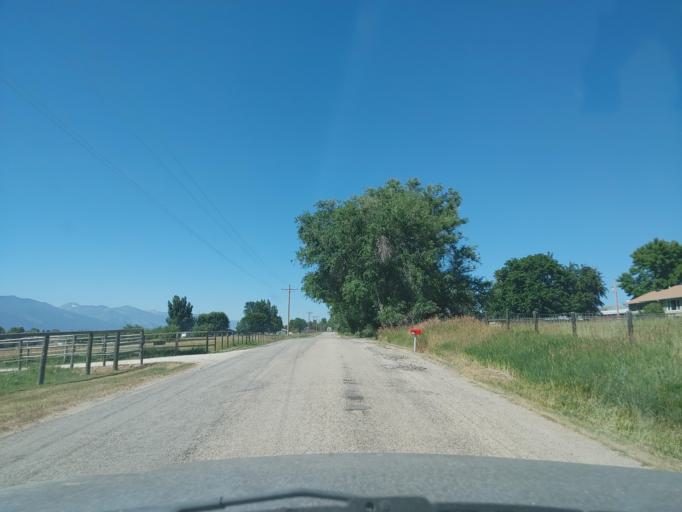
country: US
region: Montana
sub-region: Ravalli County
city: Hamilton
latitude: 46.3344
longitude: -114.0614
